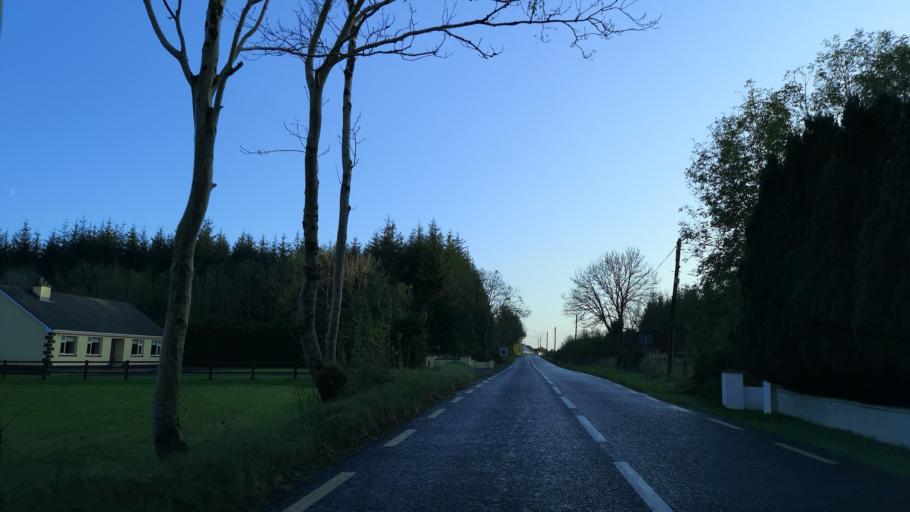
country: IE
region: Connaught
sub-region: Roscommon
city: Castlerea
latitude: 53.7204
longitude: -8.5600
